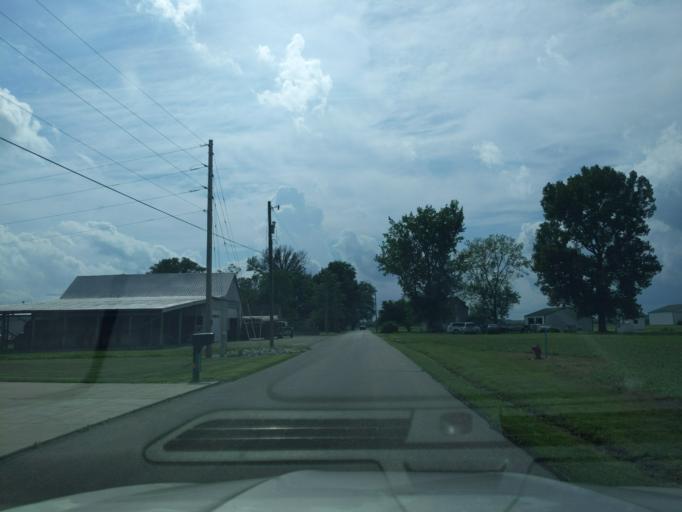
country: US
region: Indiana
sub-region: Ripley County
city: Osgood
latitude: 39.1183
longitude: -85.2950
